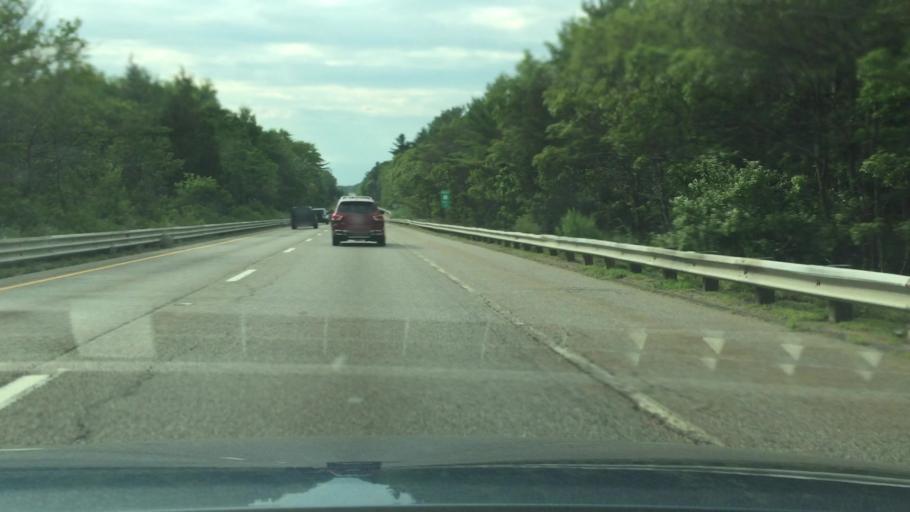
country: US
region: Massachusetts
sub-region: Plymouth County
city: Hanover
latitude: 42.1354
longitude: -70.8155
